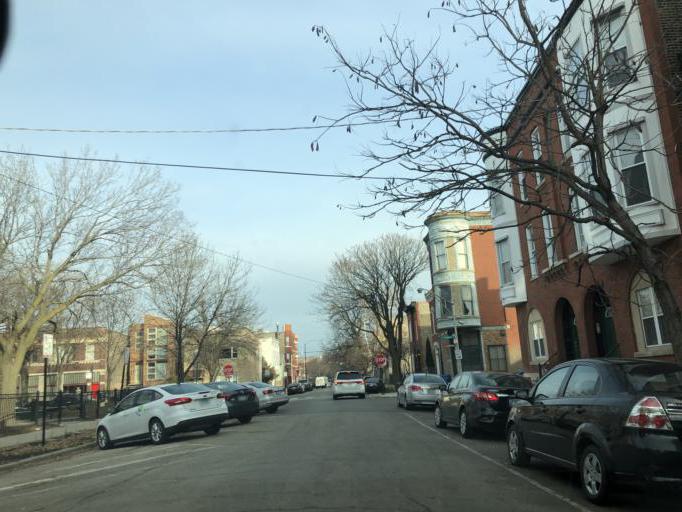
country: US
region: Illinois
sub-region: Cook County
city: Chicago
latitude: 41.8944
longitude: -87.6795
